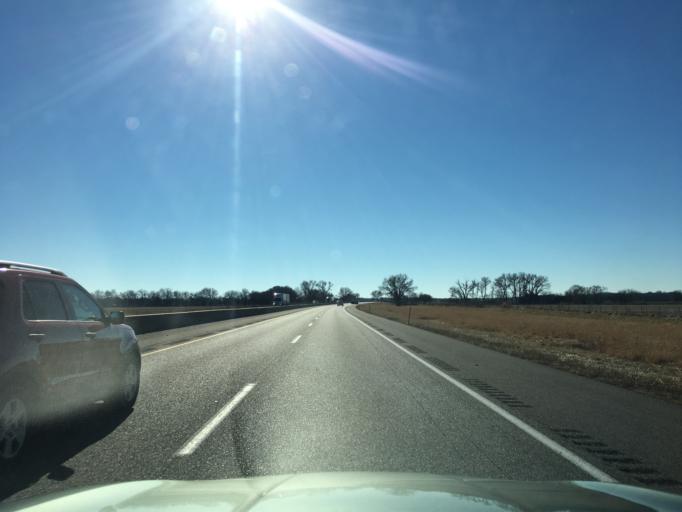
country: US
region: Kansas
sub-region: Sumner County
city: Belle Plaine
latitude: 37.4191
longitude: -97.3212
